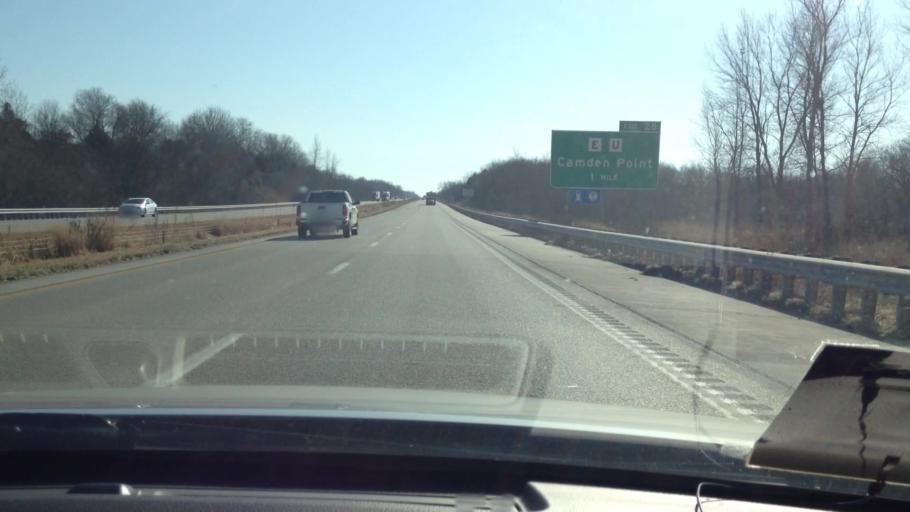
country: US
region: Missouri
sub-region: Platte County
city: Platte City
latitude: 39.4677
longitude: -94.7878
